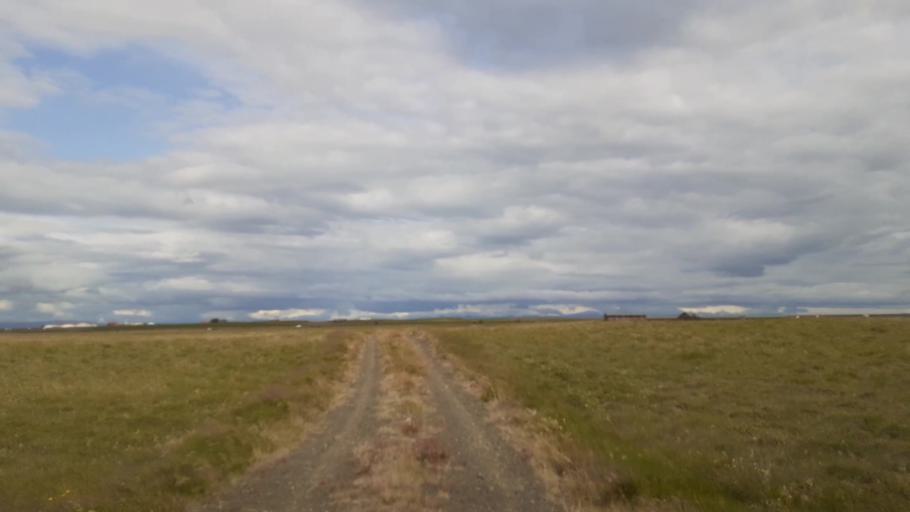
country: IS
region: South
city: Vestmannaeyjar
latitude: 63.7741
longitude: -20.2990
